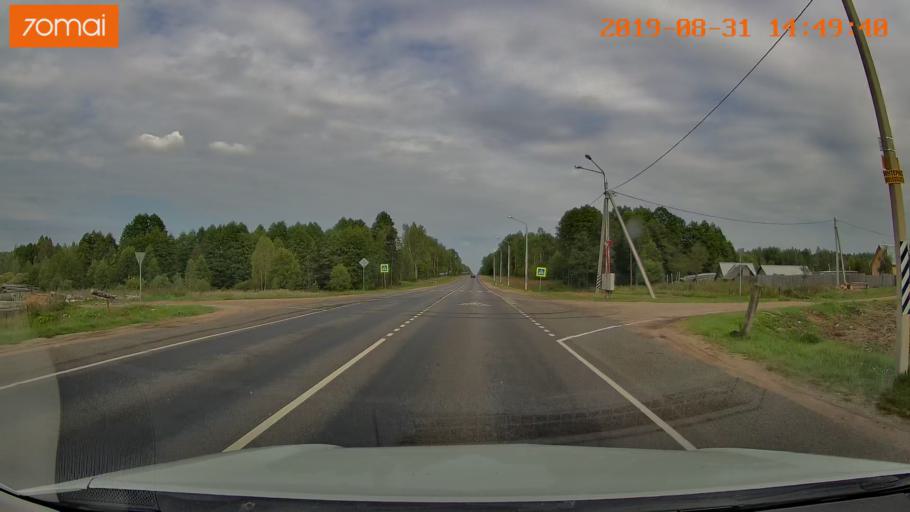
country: RU
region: Kaluga
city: Spas-Demensk
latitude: 54.2558
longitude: 33.7708
